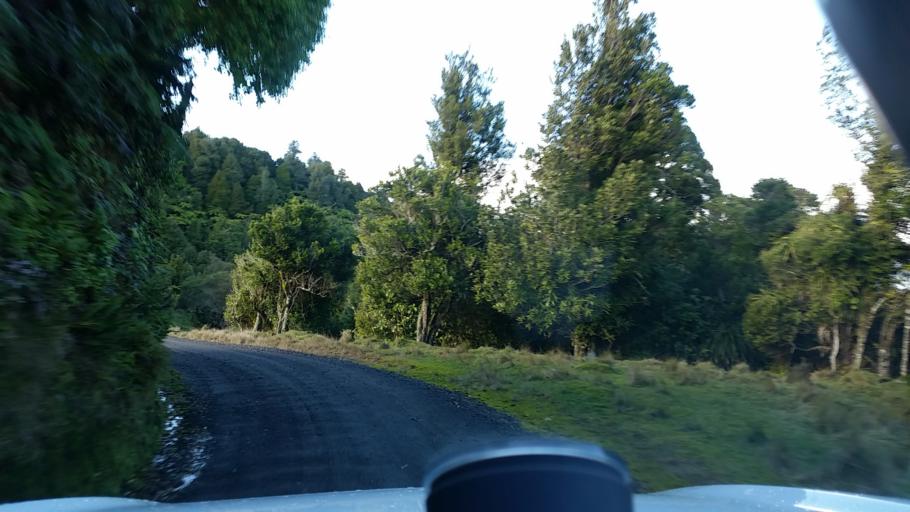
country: NZ
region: Taranaki
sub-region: South Taranaki District
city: Eltham
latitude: -39.4268
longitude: 174.5585
